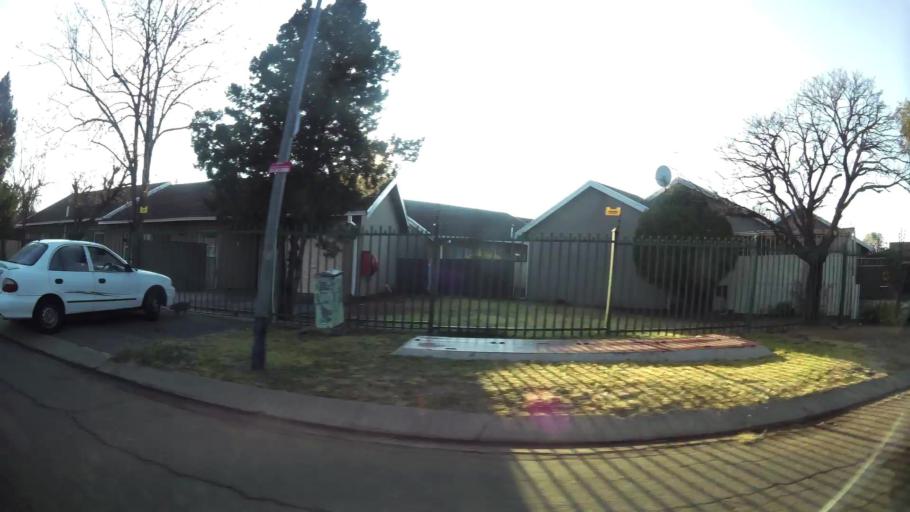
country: ZA
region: Orange Free State
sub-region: Mangaung Metropolitan Municipality
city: Bloemfontein
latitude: -29.1564
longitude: 26.1733
